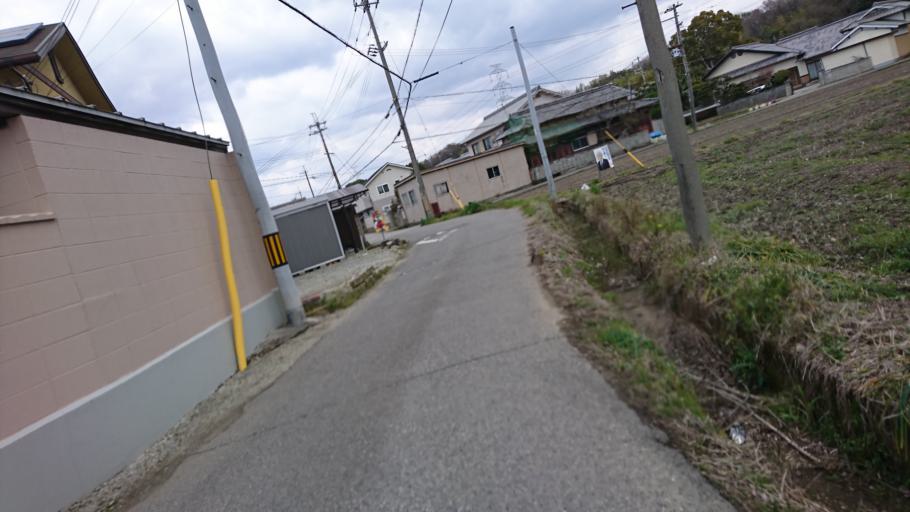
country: JP
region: Hyogo
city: Miki
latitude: 34.7688
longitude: 134.9500
